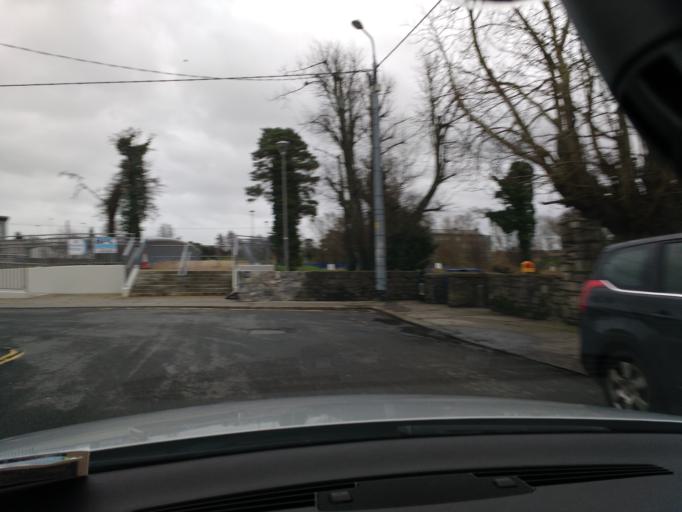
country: IE
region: Munster
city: Thurles
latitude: 52.6774
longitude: -7.8115
